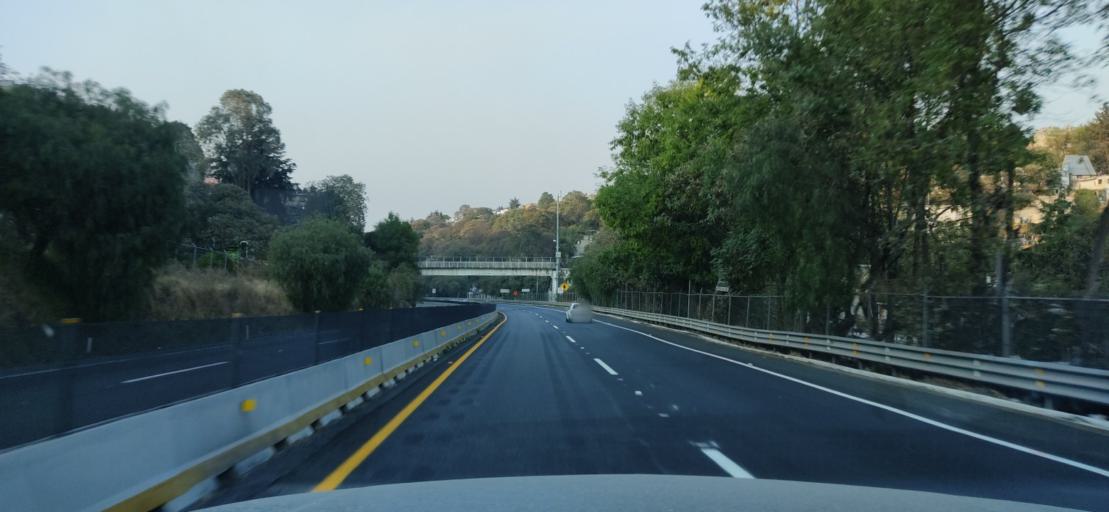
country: MX
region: Mexico City
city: Cuajimalpa
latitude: 19.3559
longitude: -99.3043
